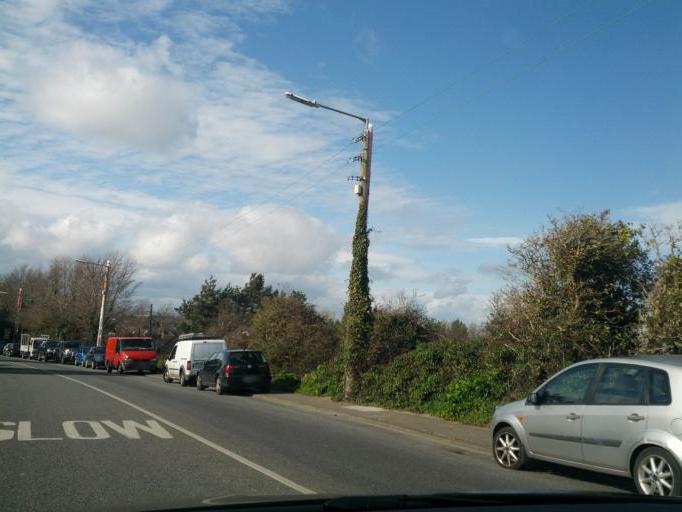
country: IE
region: Leinster
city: Sutton
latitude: 53.3792
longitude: -6.0921
